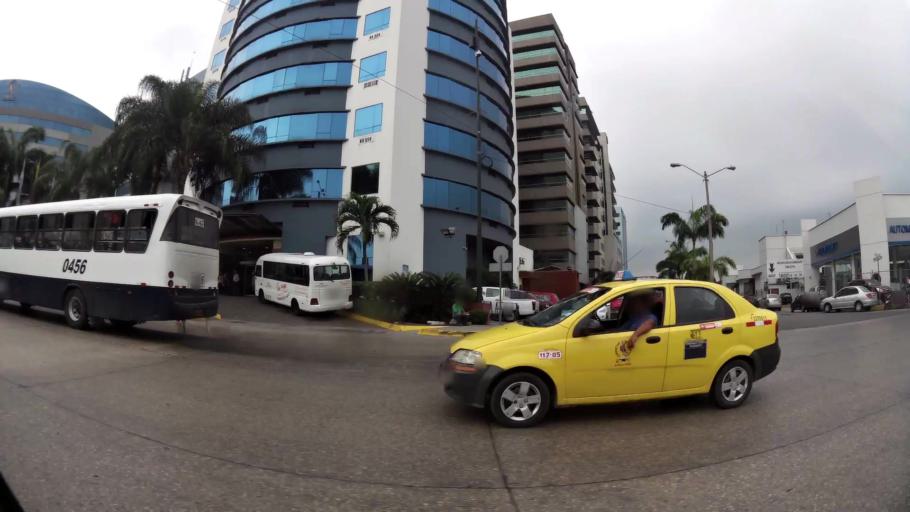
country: EC
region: Guayas
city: Eloy Alfaro
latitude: -2.1577
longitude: -79.8928
